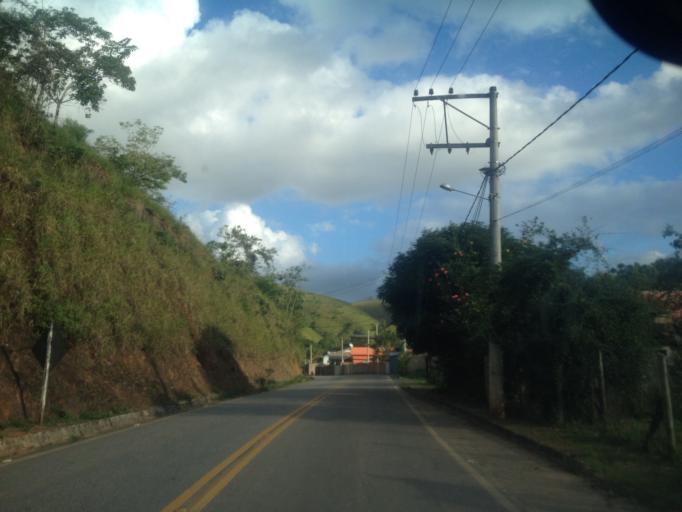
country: BR
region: Rio de Janeiro
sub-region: Quatis
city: Quatis
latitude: -22.2945
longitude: -44.2568
